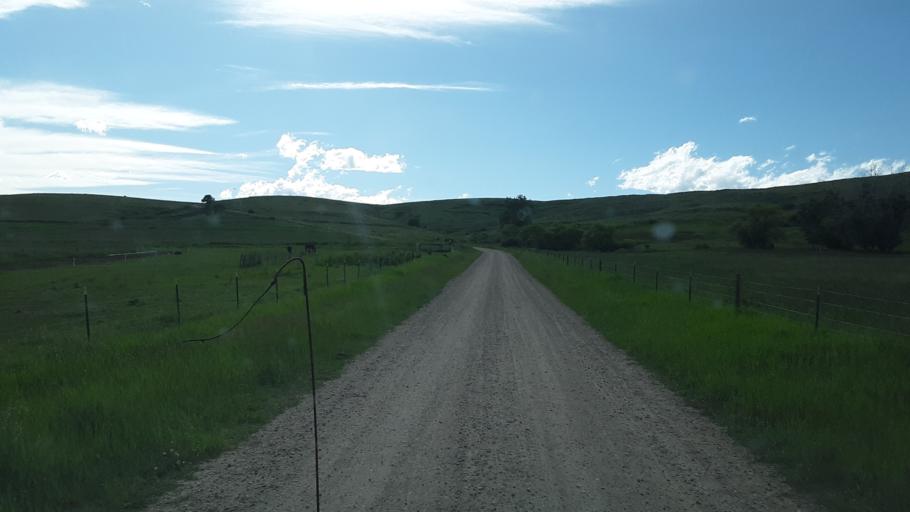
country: US
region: Montana
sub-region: Carbon County
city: Red Lodge
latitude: 45.3632
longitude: -109.1893
